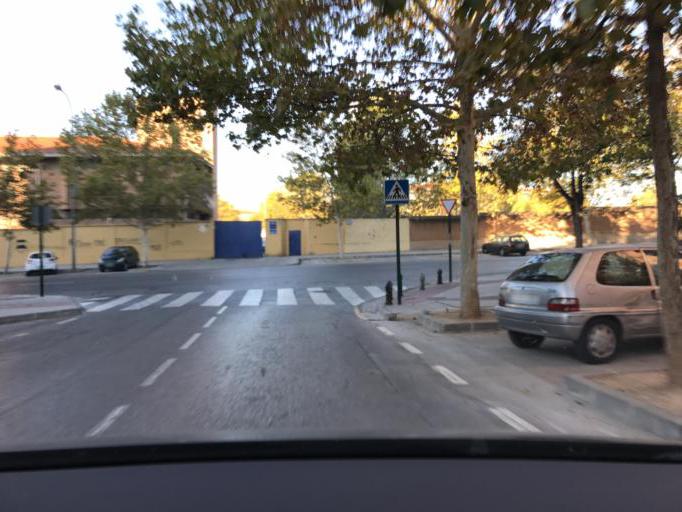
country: ES
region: Andalusia
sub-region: Provincia de Granada
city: Granada
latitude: 37.2011
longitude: -3.6040
